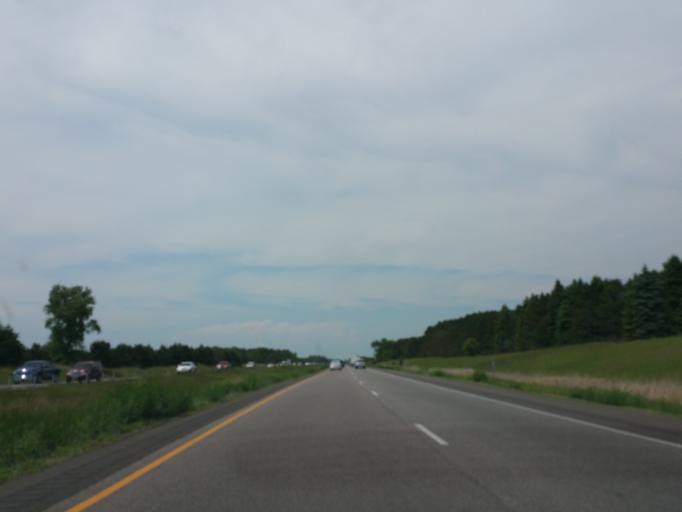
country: US
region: Minnesota
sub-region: Chisago County
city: Branch
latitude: 45.4644
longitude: -92.9961
